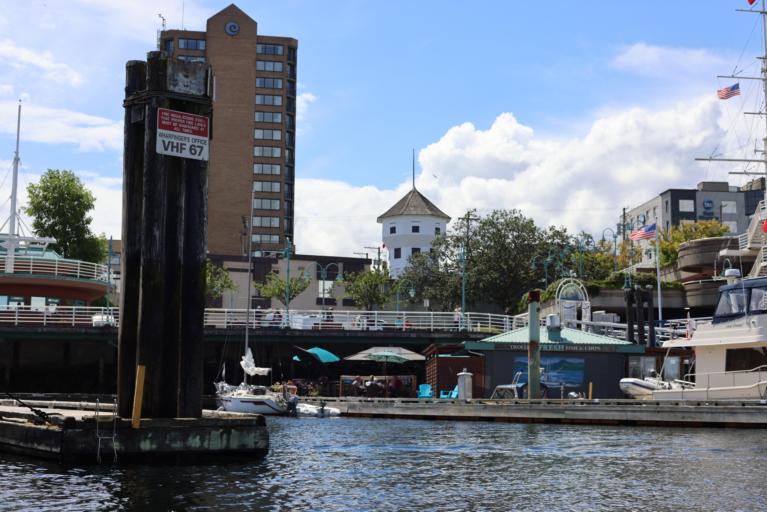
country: CA
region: British Columbia
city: Nanaimo
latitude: 49.1682
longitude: -123.9335
